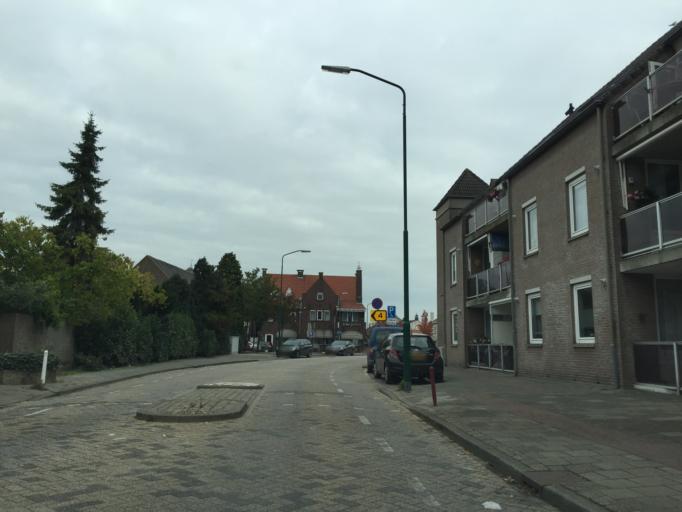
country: NL
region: North Brabant
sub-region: Gemeente Waalwijk
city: Waalwijk
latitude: 51.6611
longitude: 5.0307
